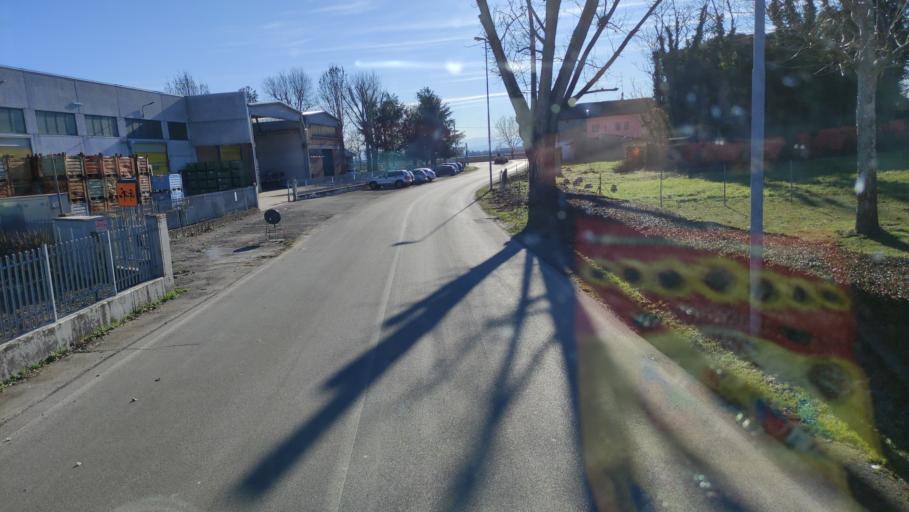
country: IT
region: Emilia-Romagna
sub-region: Provincia di Reggio Emilia
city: Campagnola Emilia
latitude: 44.8340
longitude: 10.7792
